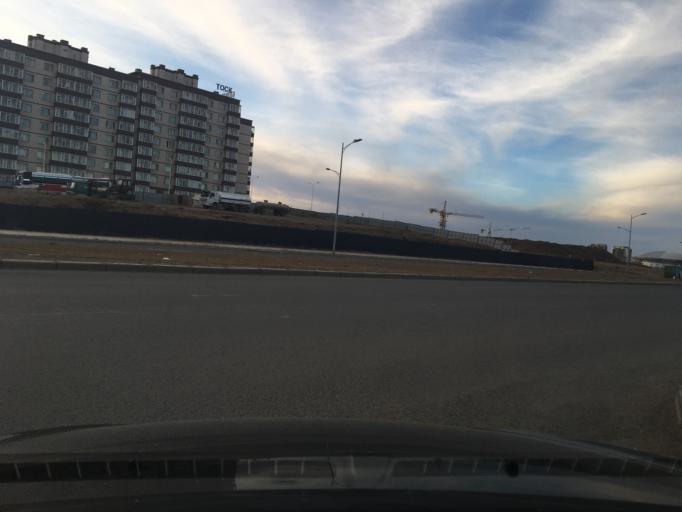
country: MN
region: Ulaanbaatar
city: Ulaanbaatar
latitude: 47.8459
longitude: 106.7910
